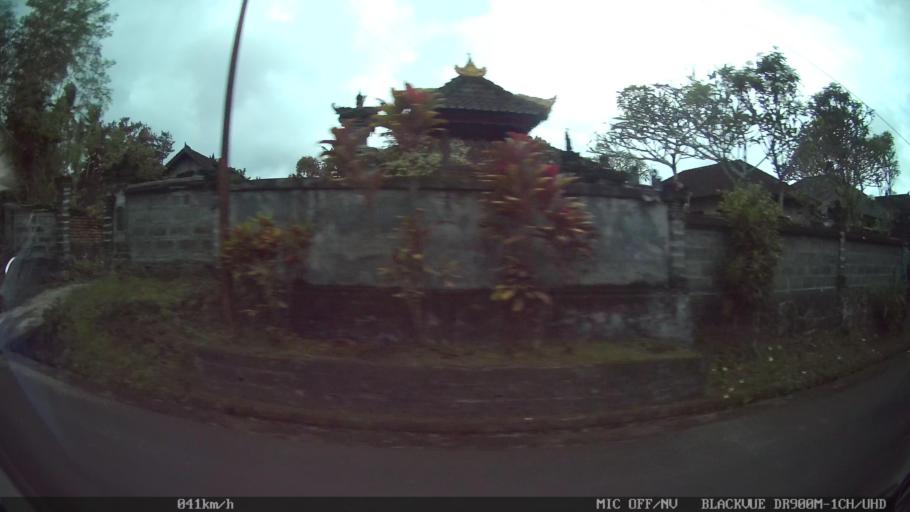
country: ID
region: Bali
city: Banjar Cemenggon
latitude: -8.5379
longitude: 115.1914
